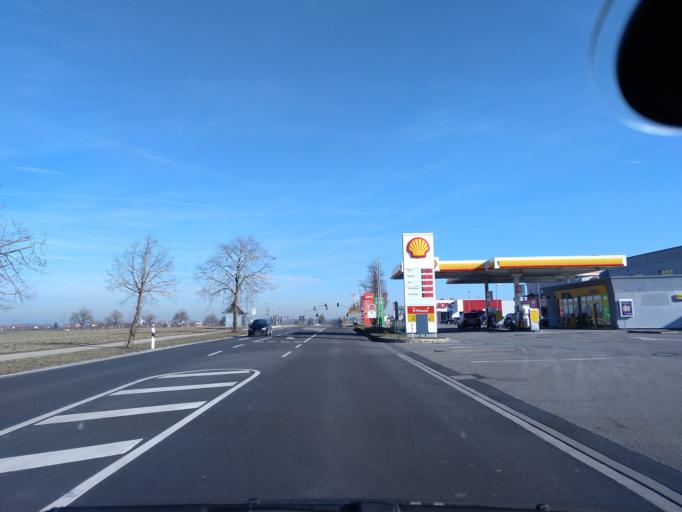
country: DE
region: Baden-Wuerttemberg
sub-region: Regierungsbezirk Stuttgart
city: Michelfeld
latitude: 49.1058
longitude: 9.7006
